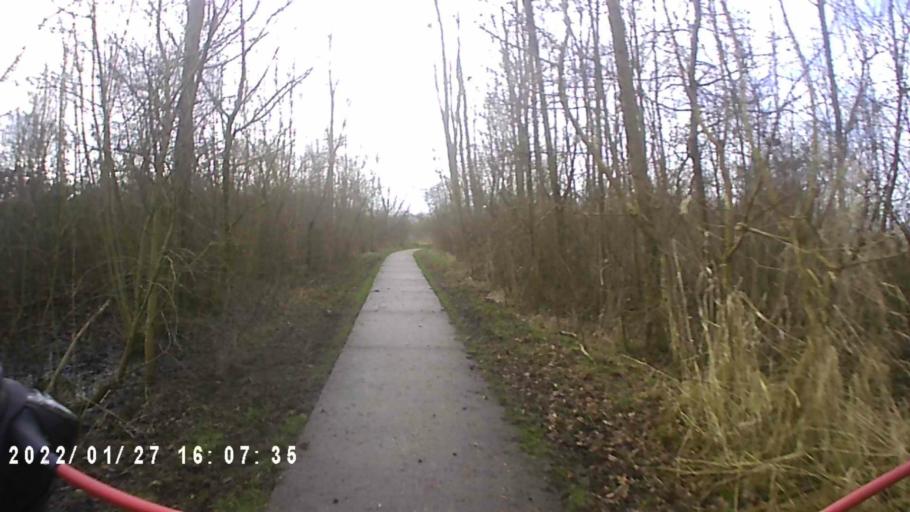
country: NL
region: Friesland
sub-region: Gemeente Dongeradeel
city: Anjum
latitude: 53.3821
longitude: 6.0878
